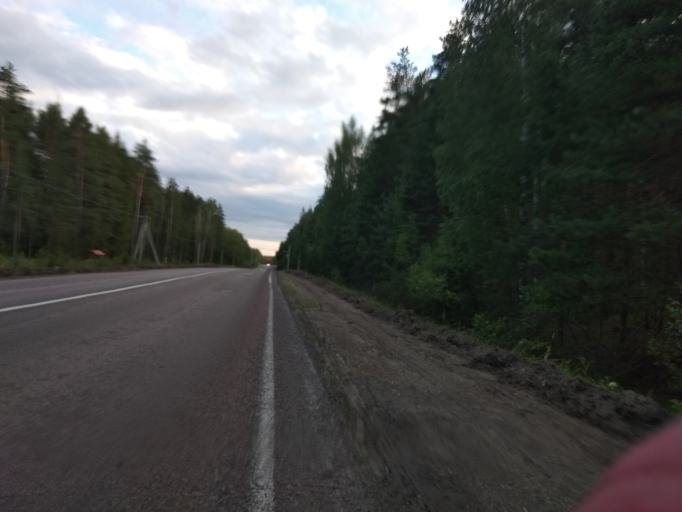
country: RU
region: Moskovskaya
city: Misheronskiy
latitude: 55.6384
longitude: 39.7509
